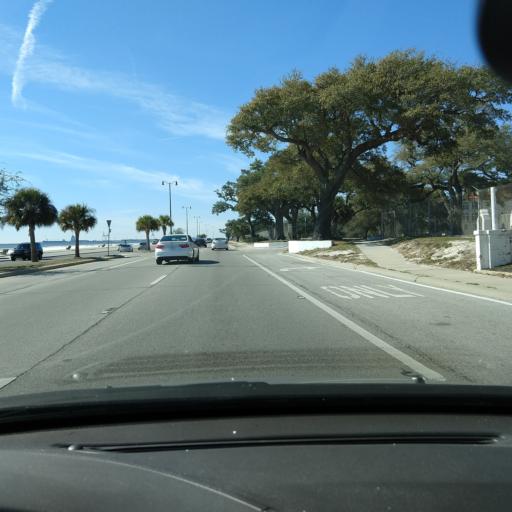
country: US
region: Mississippi
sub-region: Harrison County
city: Gulfport
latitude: 30.3768
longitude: -89.0515
